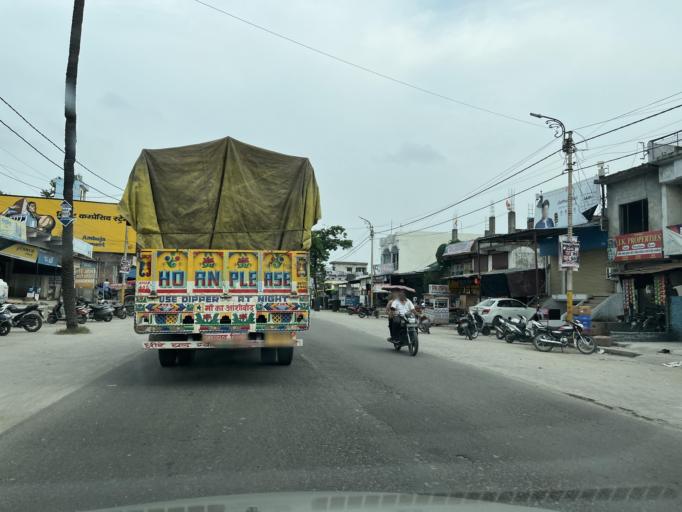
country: IN
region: Uttar Pradesh
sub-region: Rampur
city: Bilaspur
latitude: 29.0395
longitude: 79.2516
